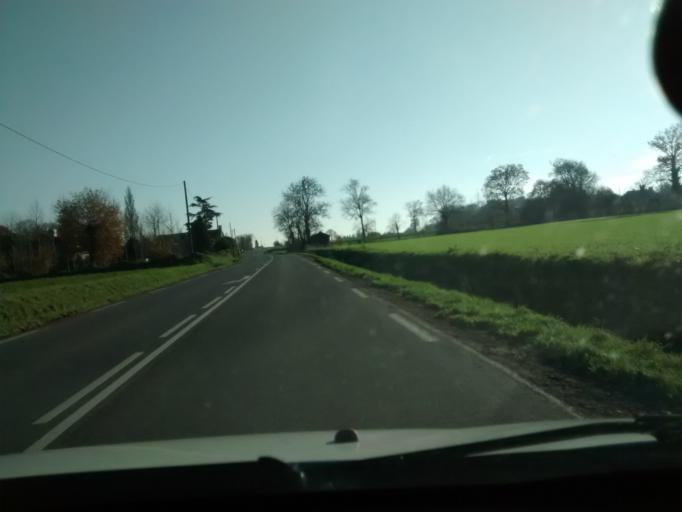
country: FR
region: Brittany
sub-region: Departement d'Ille-et-Vilaine
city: Tremblay
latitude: 48.4370
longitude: -1.4767
